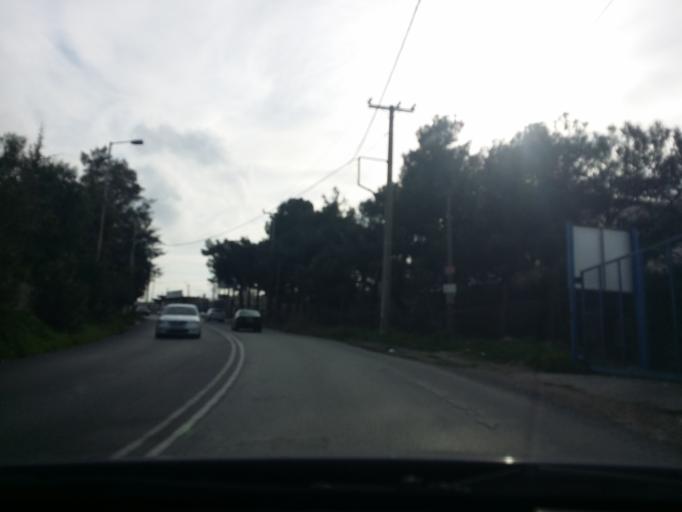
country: GR
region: Attica
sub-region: Nomarchia Athinas
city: Metamorfosi
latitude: 38.0728
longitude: 23.7598
